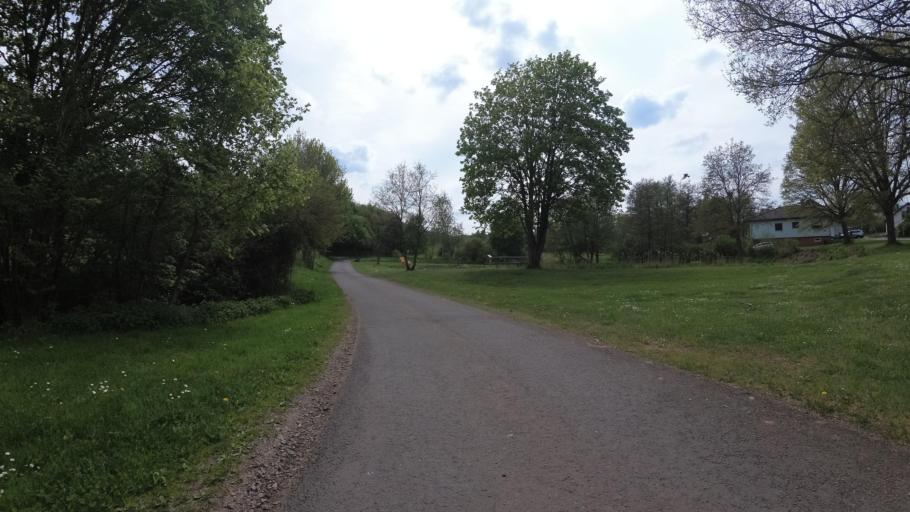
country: DE
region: Rheinland-Pfalz
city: Fohren-Linden
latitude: 49.5800
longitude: 7.2888
